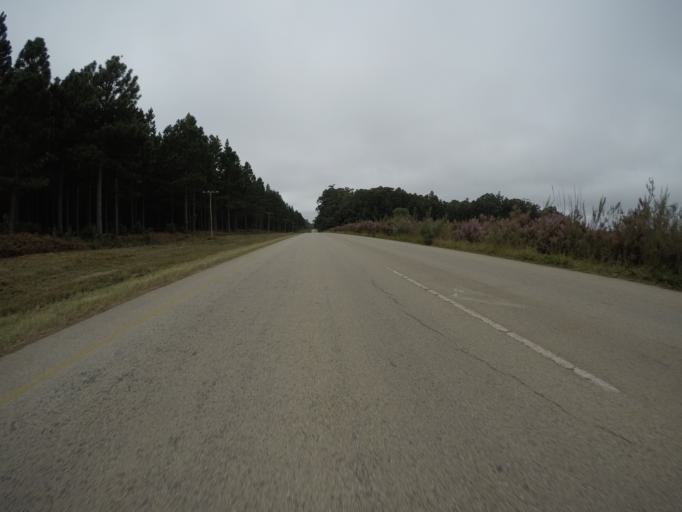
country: ZA
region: Eastern Cape
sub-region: Cacadu District Municipality
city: Kareedouw
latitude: -33.9941
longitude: 24.1075
